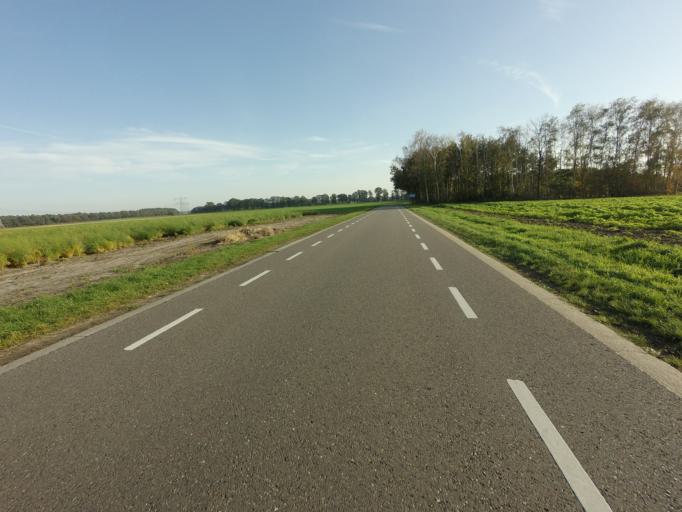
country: NL
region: Limburg
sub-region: Gemeente Roerdalen
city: Montfort
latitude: 51.1120
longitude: 5.9758
